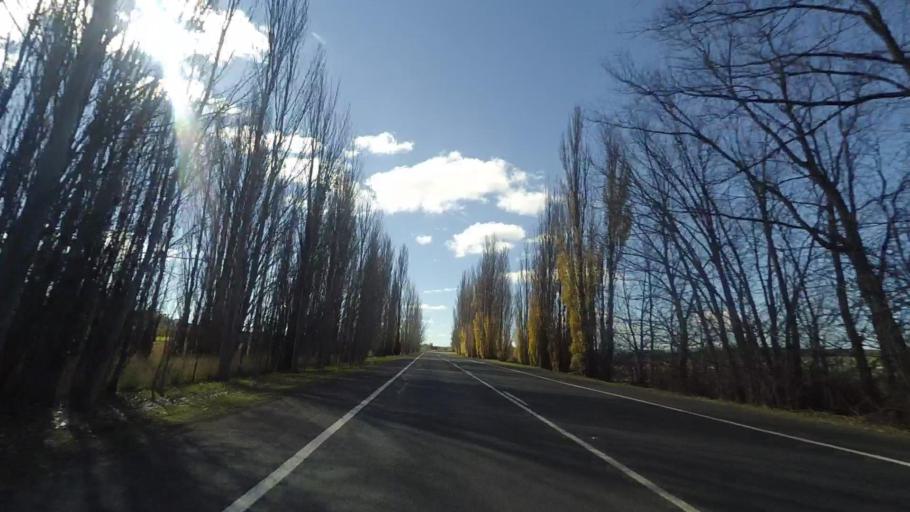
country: AU
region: New South Wales
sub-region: Bathurst Regional
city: Perthville
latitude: -33.4612
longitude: 149.5724
